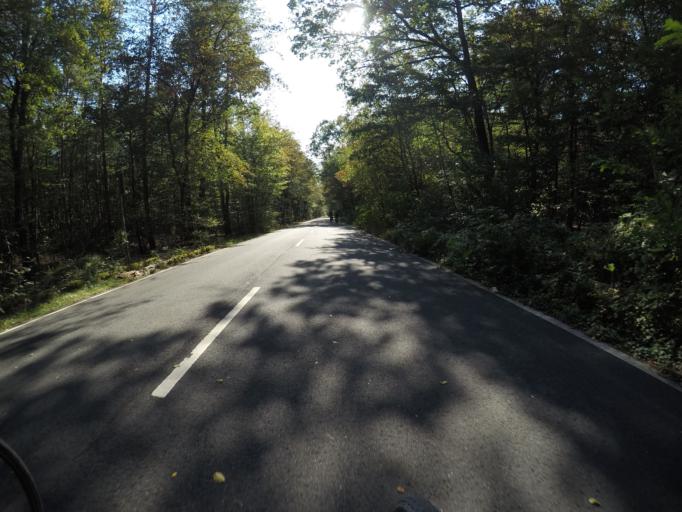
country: DE
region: Hesse
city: Niederrad
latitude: 50.0715
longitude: 8.6637
